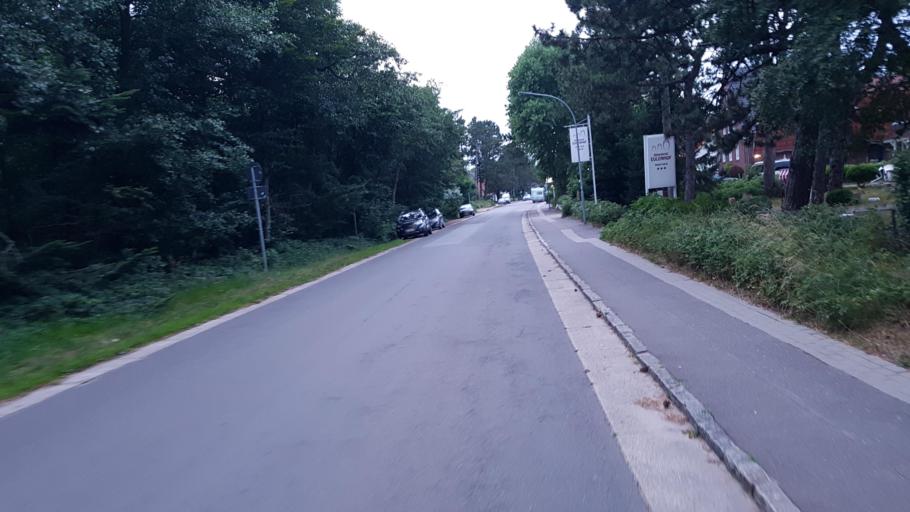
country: DE
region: Schleswig-Holstein
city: Sankt Peter-Ording
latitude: 54.3081
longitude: 8.6185
